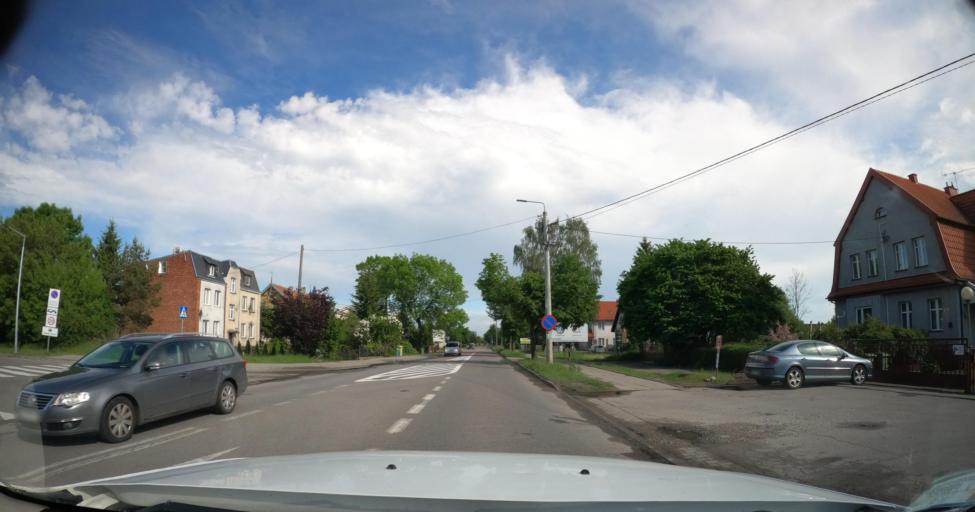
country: PL
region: Warmian-Masurian Voivodeship
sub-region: Powiat elblaski
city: Elblag
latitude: 54.1653
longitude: 19.3771
